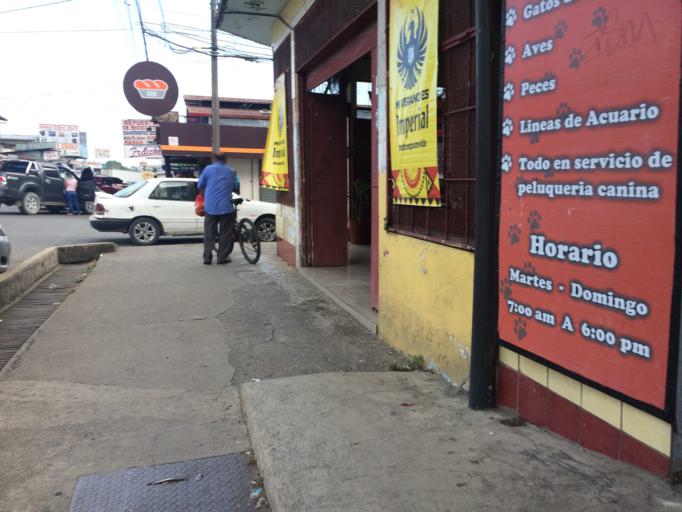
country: CR
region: Puntarenas
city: Canoas
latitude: 8.5326
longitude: -82.8386
